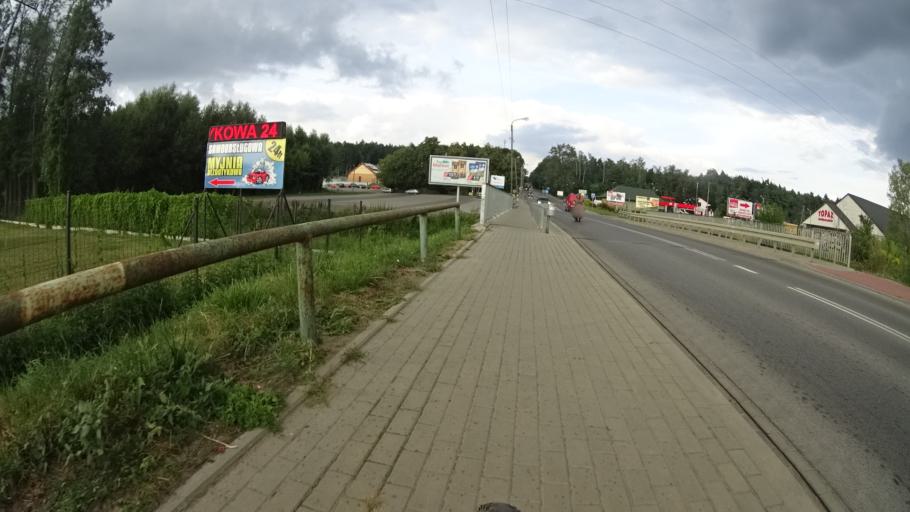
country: PL
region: Masovian Voivodeship
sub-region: Powiat grojecki
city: Mogielnica
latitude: 51.6956
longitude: 20.7254
